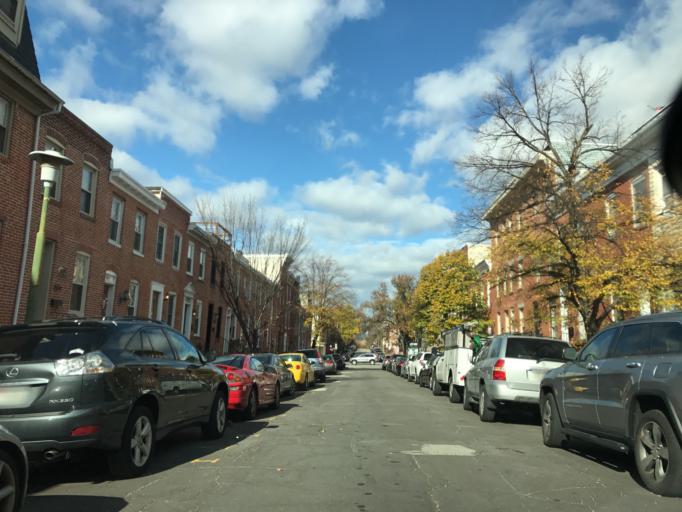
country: US
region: Maryland
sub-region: City of Baltimore
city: Baltimore
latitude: 39.2720
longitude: -76.6099
